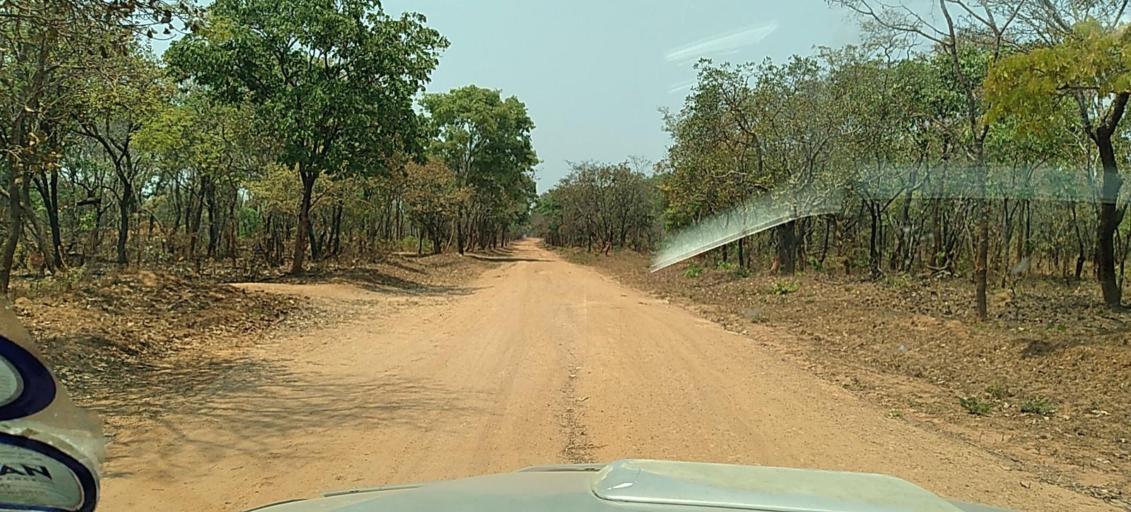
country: ZM
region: North-Western
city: Kasempa
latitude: -13.5651
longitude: 26.0930
